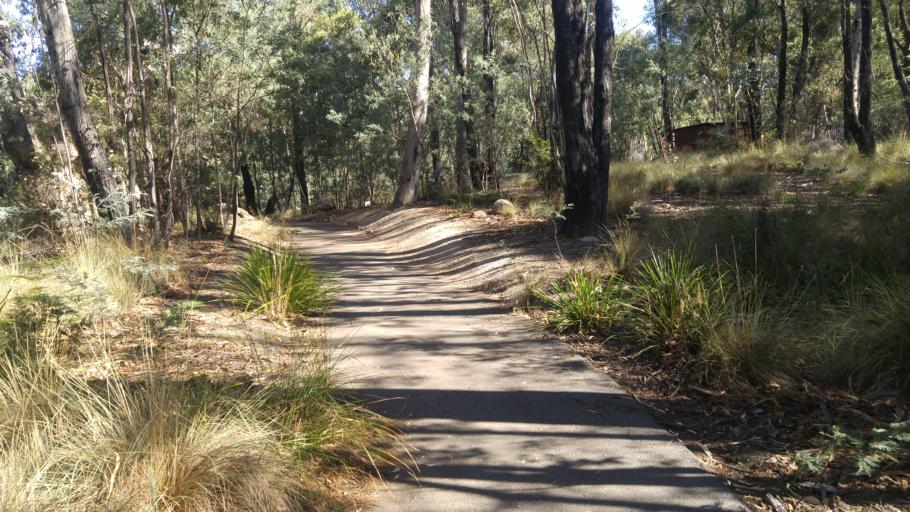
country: AU
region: Australian Capital Territory
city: Macarthur
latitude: -35.4665
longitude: 148.9047
